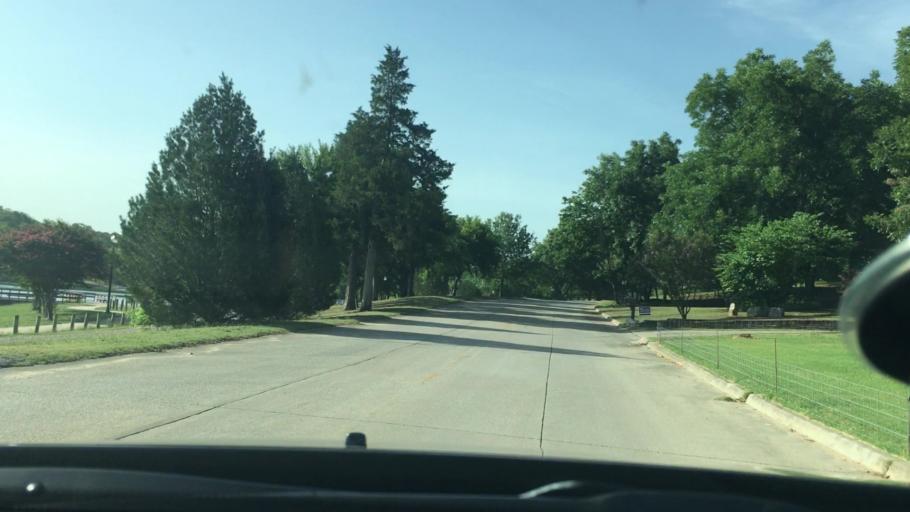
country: US
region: Oklahoma
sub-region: Pontotoc County
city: Ada
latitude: 34.7636
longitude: -96.6558
